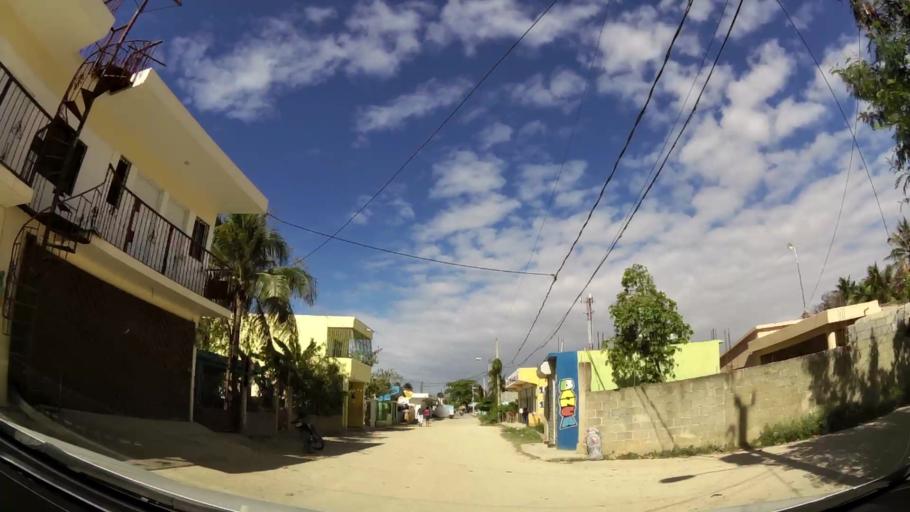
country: DO
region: Santo Domingo
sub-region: Santo Domingo
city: Boca Chica
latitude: 18.4595
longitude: -69.6041
